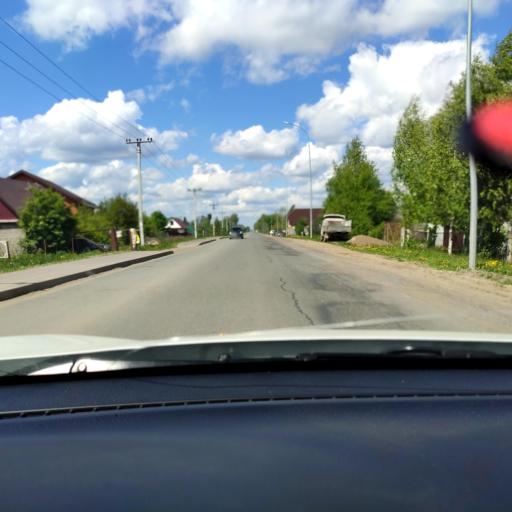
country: RU
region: Tatarstan
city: Stolbishchi
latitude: 55.6968
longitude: 49.1924
